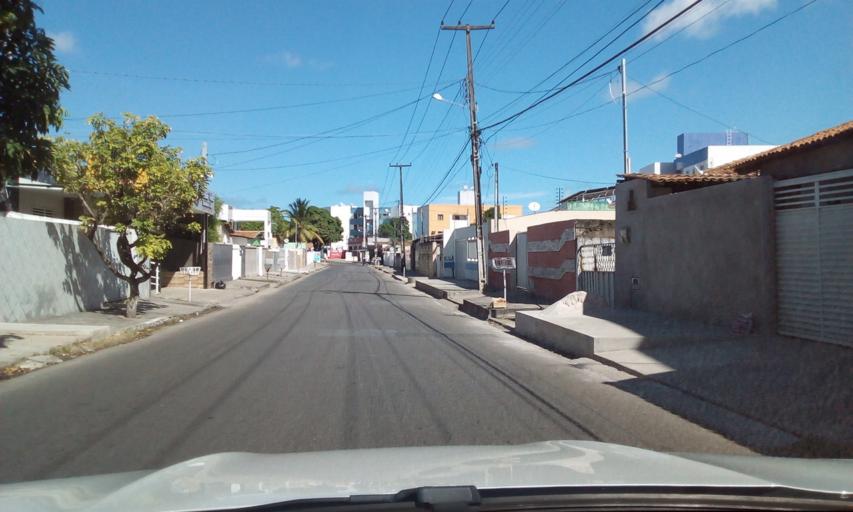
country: BR
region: Paraiba
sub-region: Joao Pessoa
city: Joao Pessoa
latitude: -7.1811
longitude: -34.8630
